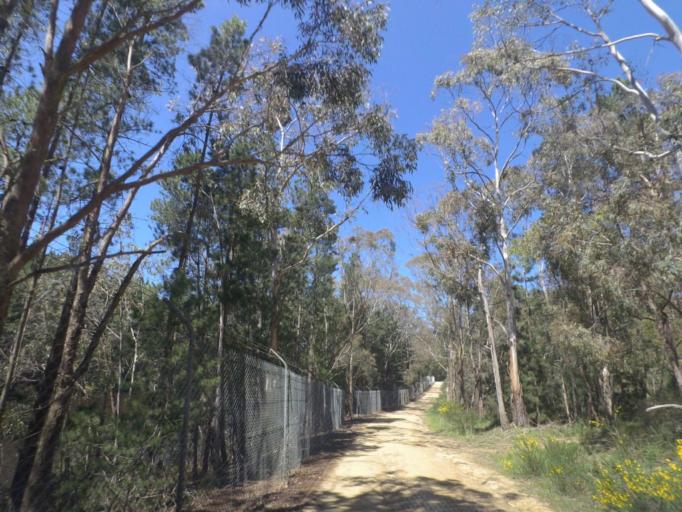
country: AU
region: Victoria
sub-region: Hume
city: Sunbury
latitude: -37.3951
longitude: 144.5566
